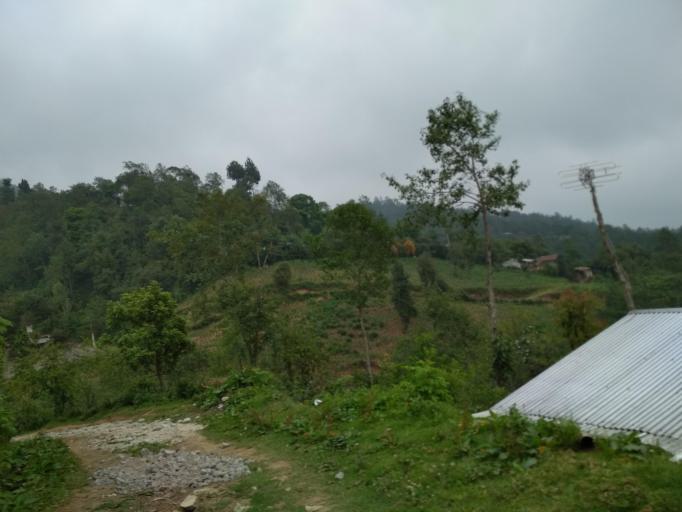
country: MX
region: Veracruz
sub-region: La Perla
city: Chilapa
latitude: 18.9903
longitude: -97.1551
